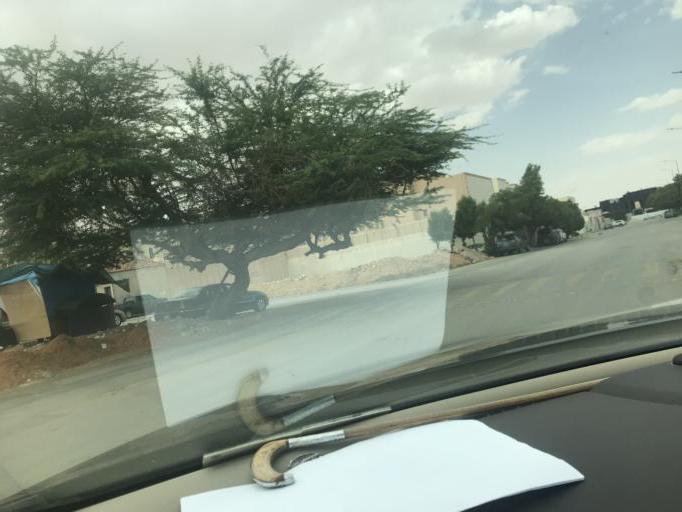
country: SA
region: Ar Riyad
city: Riyadh
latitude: 24.7290
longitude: 46.7804
